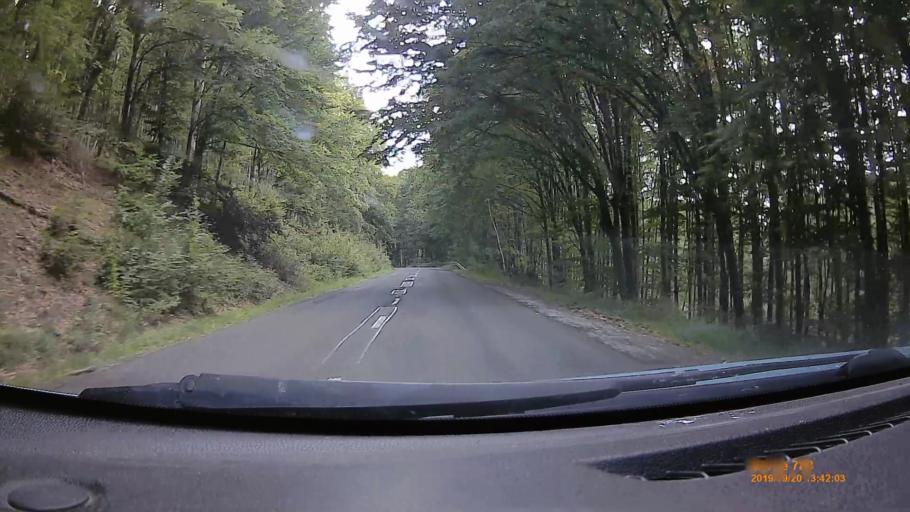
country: HU
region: Heves
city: Szilvasvarad
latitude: 48.0587
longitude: 20.5416
